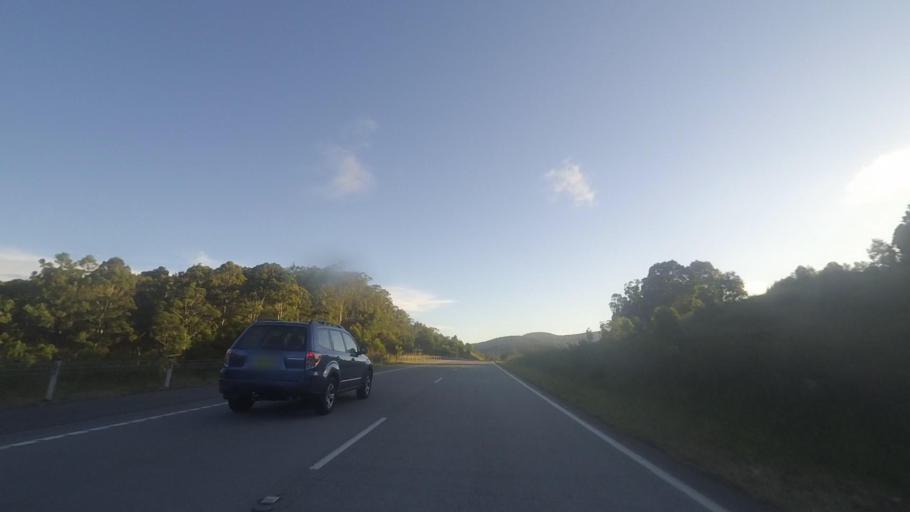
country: AU
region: New South Wales
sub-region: Great Lakes
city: Bulahdelah
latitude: -32.4739
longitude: 152.1952
